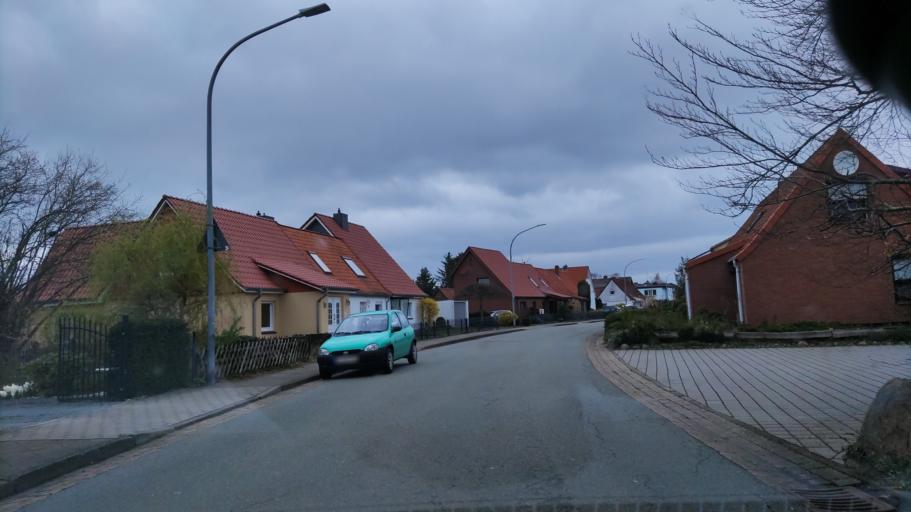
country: DE
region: Lower Saxony
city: Winsen
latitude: 53.3574
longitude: 10.2193
